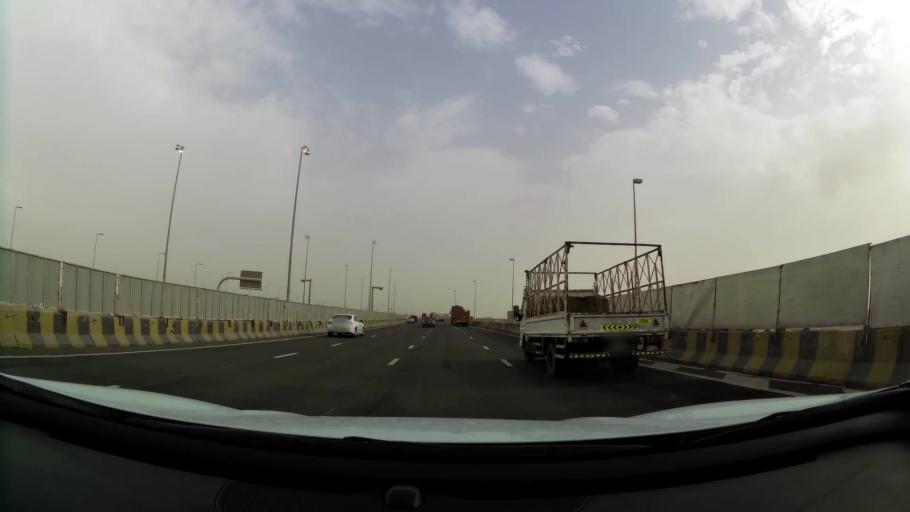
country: AE
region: Abu Dhabi
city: Abu Dhabi
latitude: 24.4572
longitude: 54.6262
